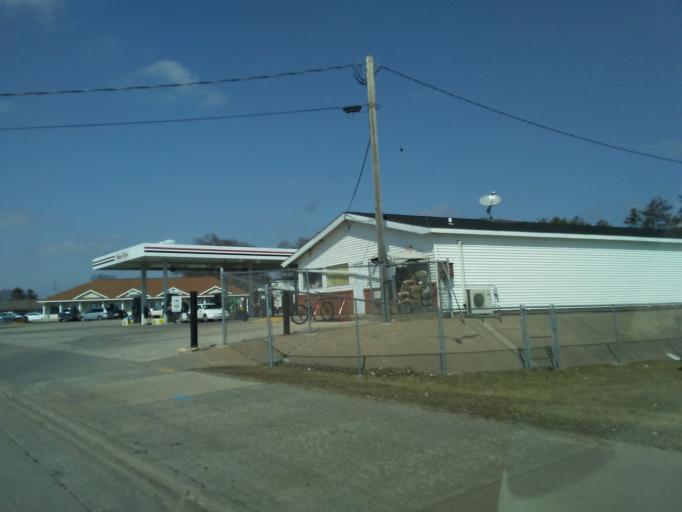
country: US
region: Wisconsin
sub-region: La Crosse County
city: La Crosse
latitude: 43.7671
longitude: -91.2116
